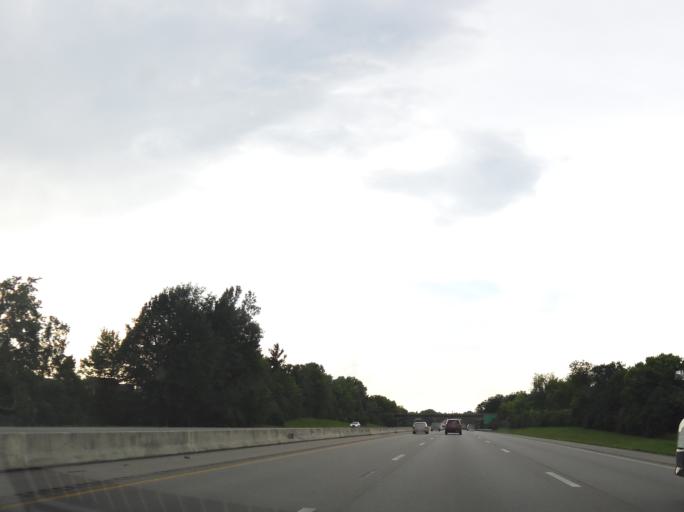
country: US
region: Kentucky
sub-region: Fayette County
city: Lexington
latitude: 37.9937
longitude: -84.3957
